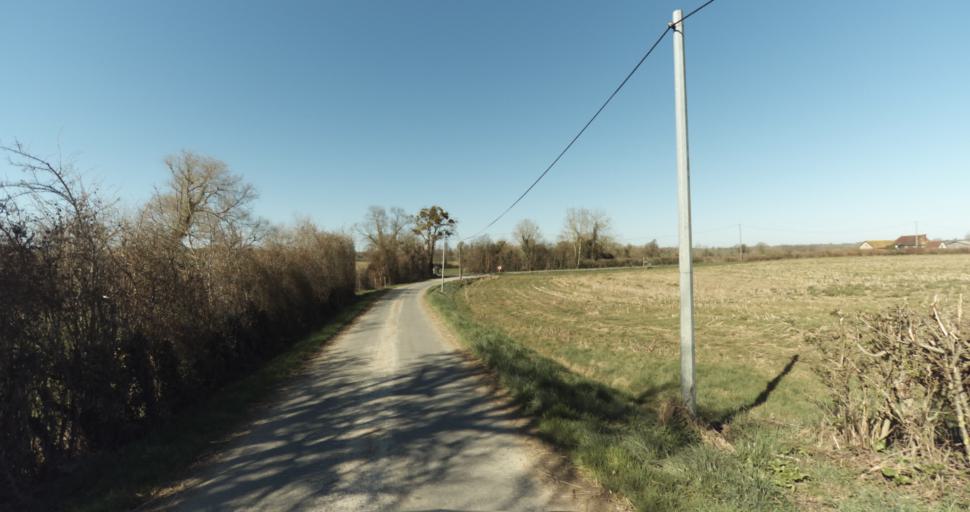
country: FR
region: Lower Normandy
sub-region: Departement de l'Orne
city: Trun
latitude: 48.9189
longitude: 0.0307
